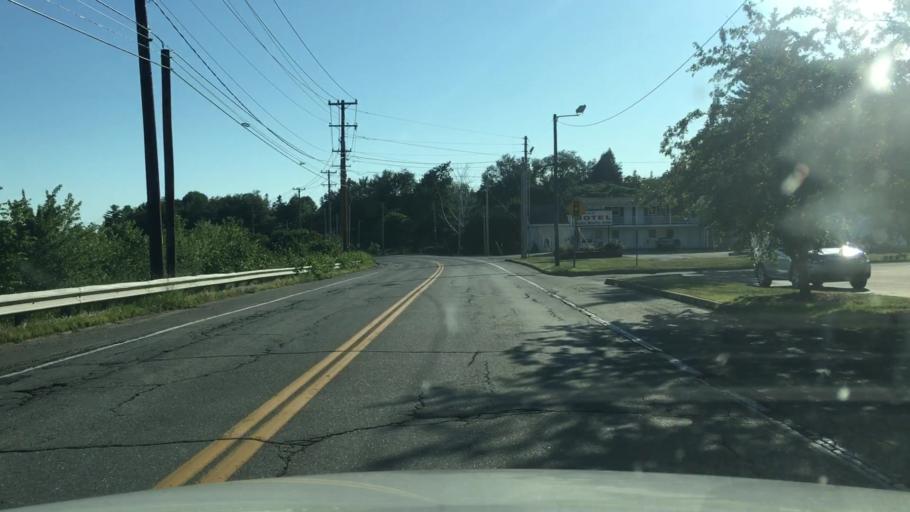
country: US
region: Maine
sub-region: Penobscot County
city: Brewer
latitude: 44.8158
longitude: -68.7352
